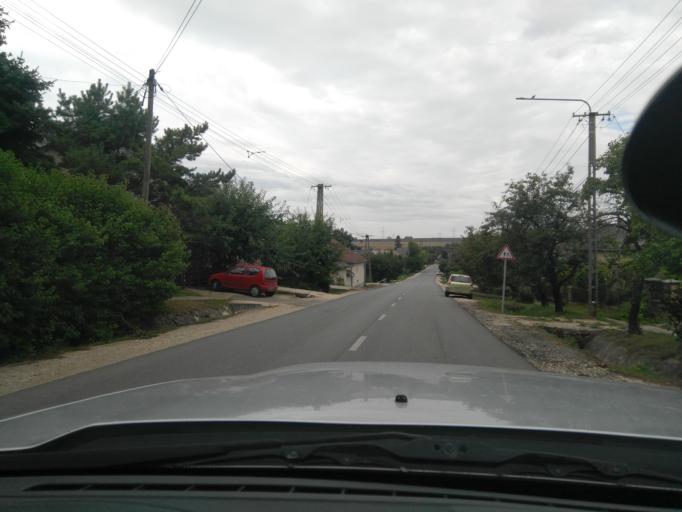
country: HU
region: Fejer
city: Martonvasar
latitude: 47.3453
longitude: 18.7537
